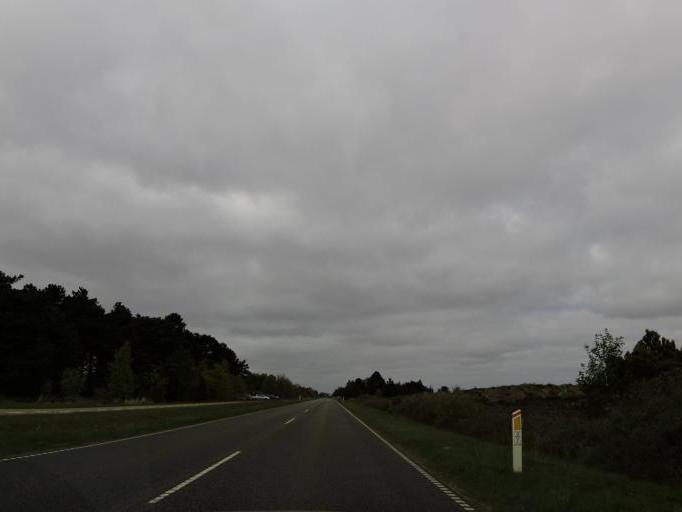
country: DE
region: Schleswig-Holstein
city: List
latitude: 55.1192
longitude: 8.5468
